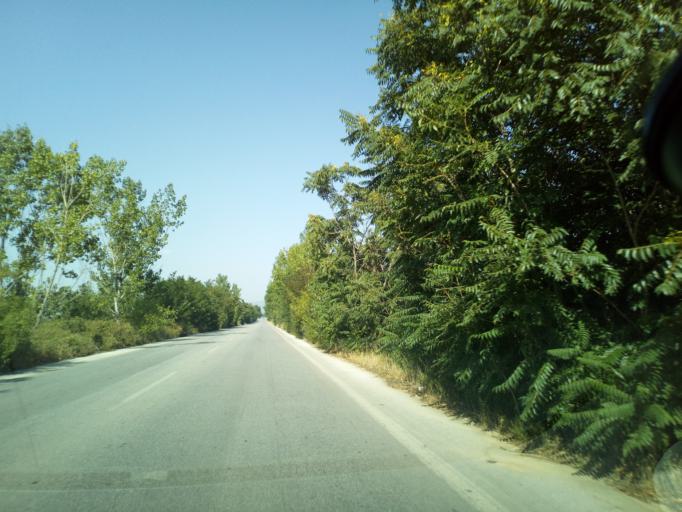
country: GR
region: Central Macedonia
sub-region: Nomos Thessalonikis
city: Gerakarou
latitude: 40.6371
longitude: 23.2606
